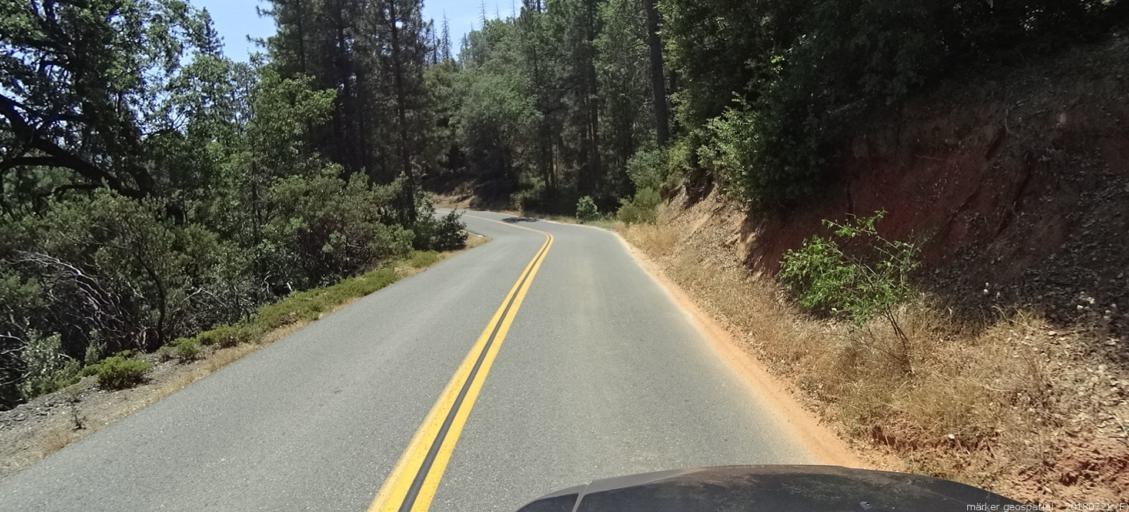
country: US
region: California
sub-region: Madera County
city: Oakhurst
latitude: 37.2779
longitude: -119.5353
